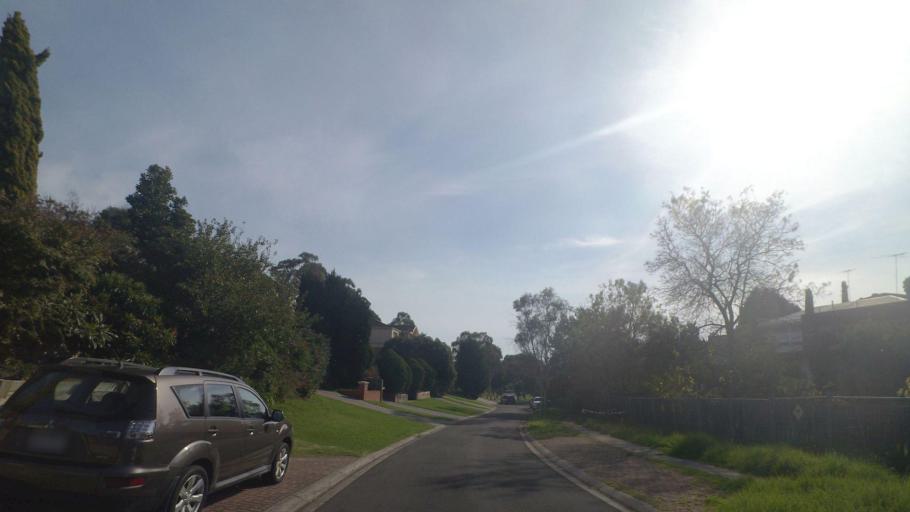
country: AU
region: Victoria
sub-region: Manningham
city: Doncaster East
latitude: -37.7718
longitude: 145.1445
